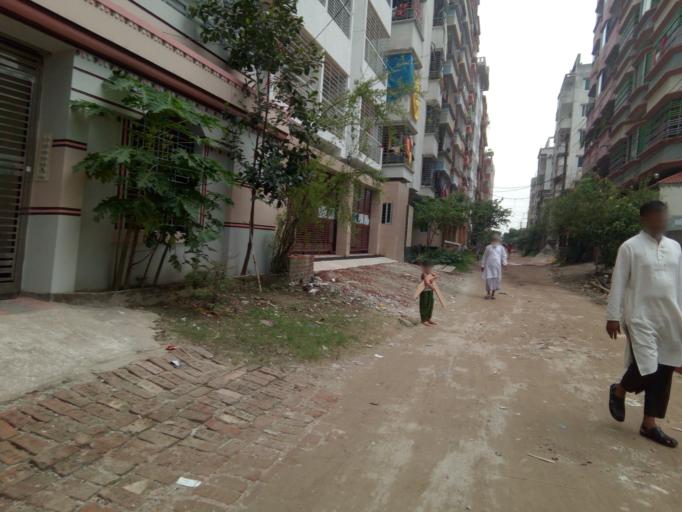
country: BD
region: Dhaka
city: Paltan
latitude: 23.7568
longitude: 90.4422
